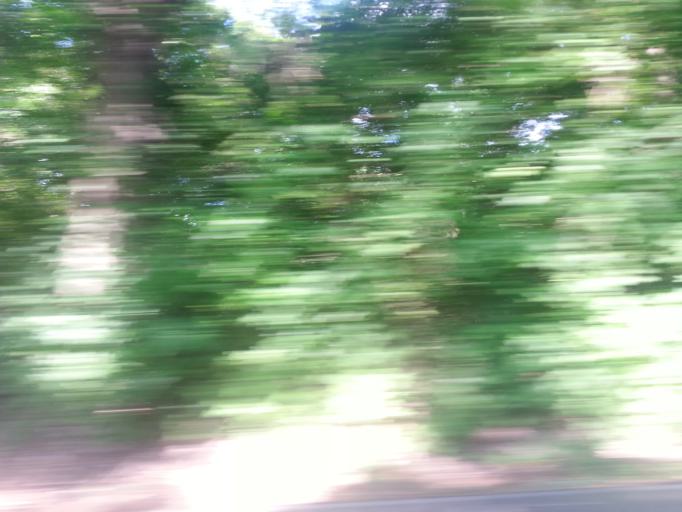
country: US
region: Tennessee
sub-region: Knox County
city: Knoxville
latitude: 36.0846
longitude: -83.8986
